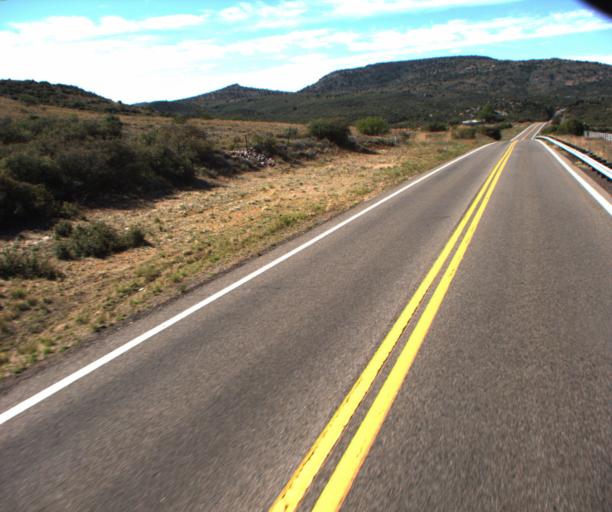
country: US
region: Arizona
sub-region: Yavapai County
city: Congress
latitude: 34.2448
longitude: -112.7366
